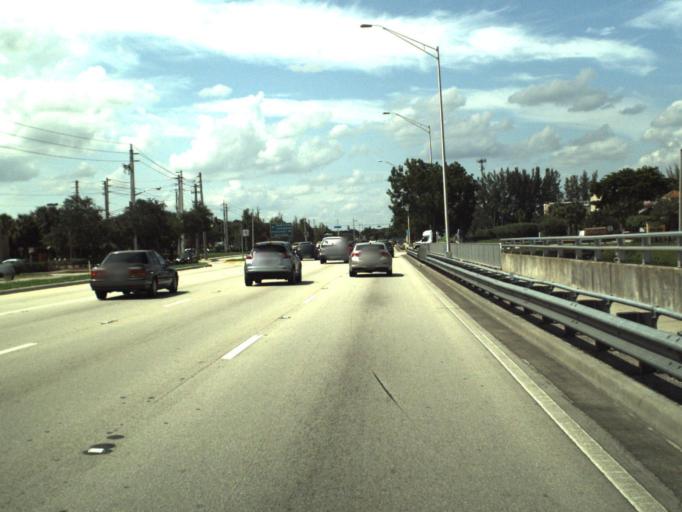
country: US
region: Florida
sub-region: Broward County
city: Pembroke Pines
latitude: 26.0110
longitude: -80.2481
